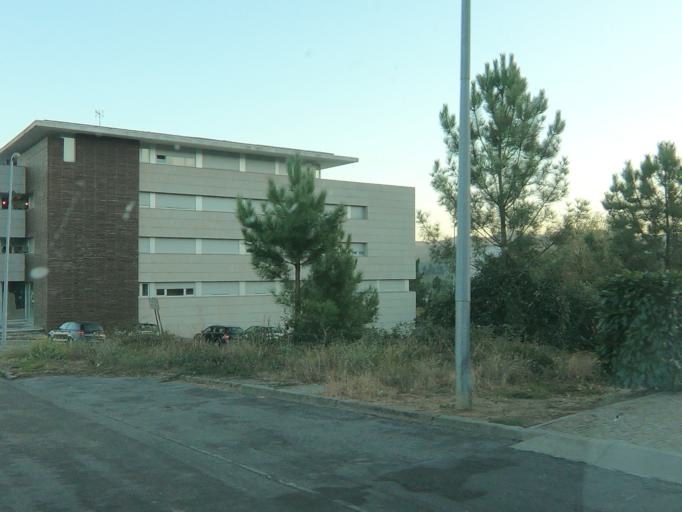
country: PT
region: Vila Real
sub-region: Vila Real
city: Vila Real
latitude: 41.3056
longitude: -7.7659
